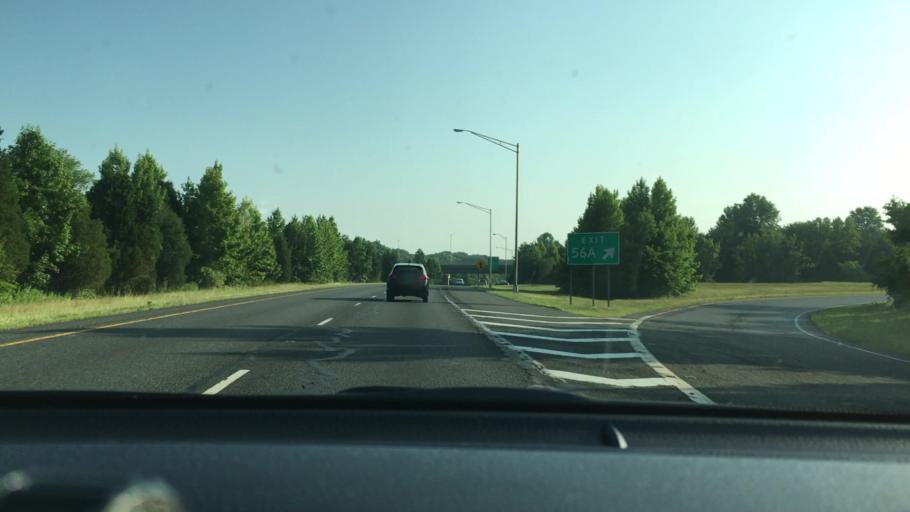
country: US
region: New Jersey
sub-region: Gloucester County
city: Wenonah
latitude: 39.7912
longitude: -75.1154
